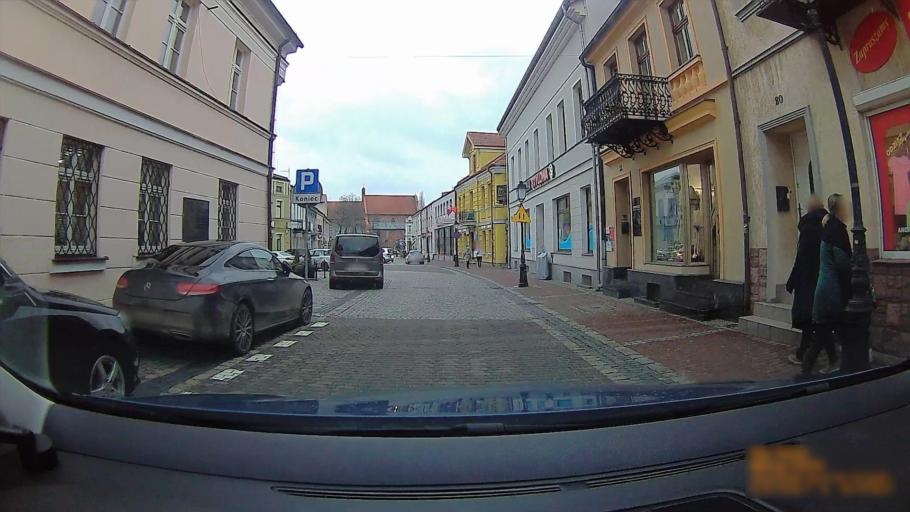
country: PL
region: Greater Poland Voivodeship
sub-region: Konin
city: Konin
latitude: 52.2103
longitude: 18.2544
